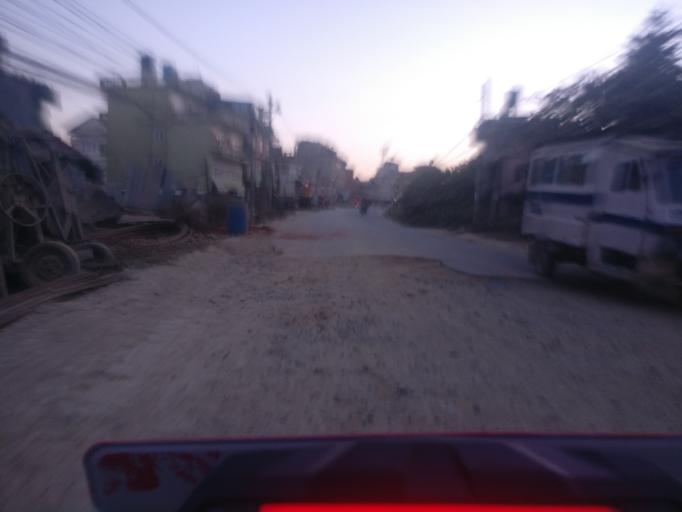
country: NP
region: Central Region
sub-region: Bagmati Zone
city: Patan
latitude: 27.6497
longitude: 85.3208
